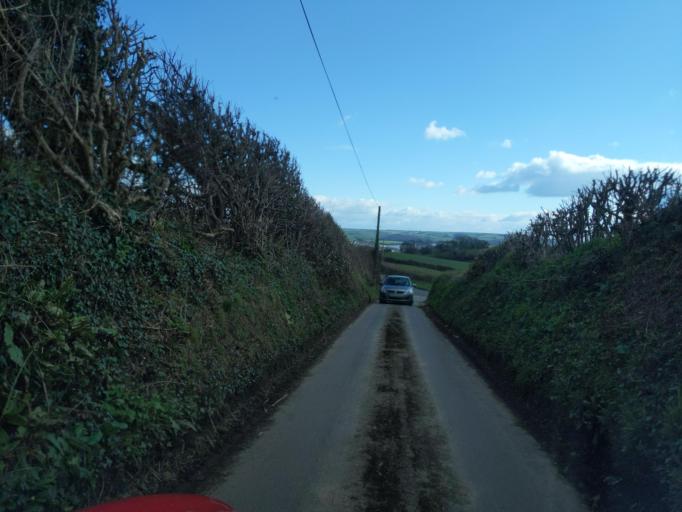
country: GB
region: England
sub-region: Devon
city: Kingsbridge
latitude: 50.2957
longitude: -3.7890
